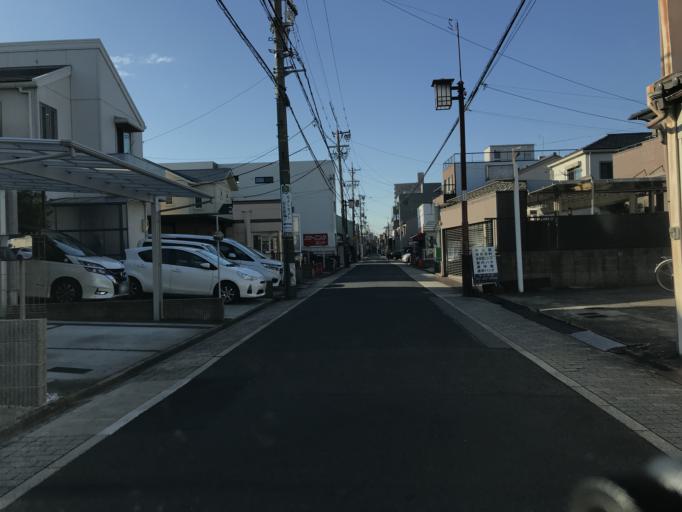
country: JP
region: Aichi
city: Nagoya-shi
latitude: 35.1882
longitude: 136.8808
